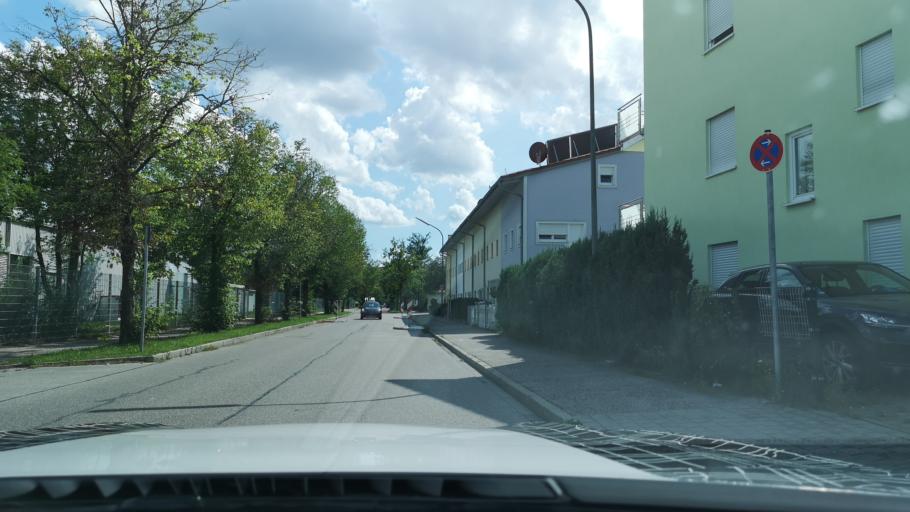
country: DE
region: Bavaria
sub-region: Upper Bavaria
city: Garching bei Munchen
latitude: 48.2497
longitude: 11.6128
